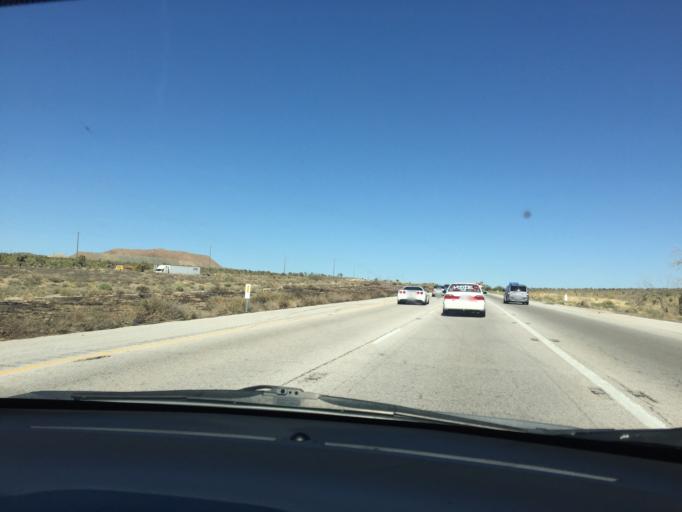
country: US
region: Nevada
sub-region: Clark County
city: Sandy Valley
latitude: 35.4718
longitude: -115.5607
